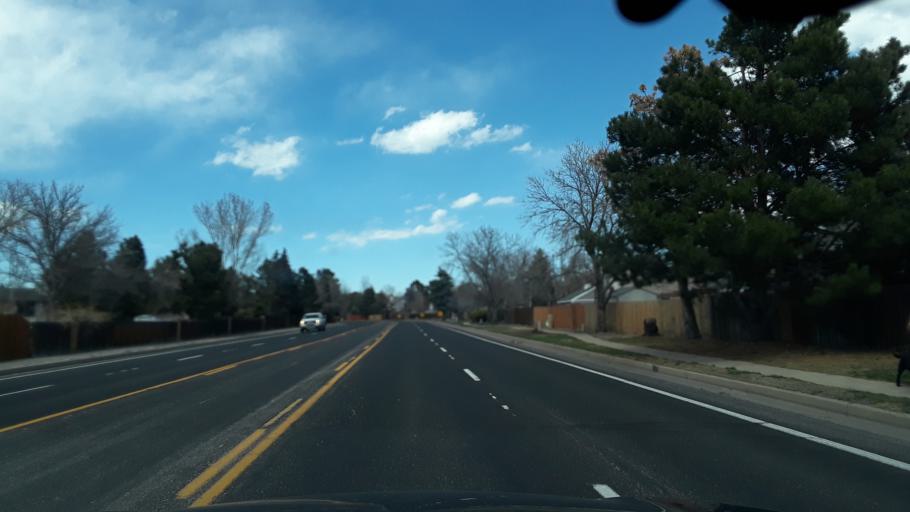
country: US
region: Colorado
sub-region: El Paso County
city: Black Forest
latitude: 38.9490
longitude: -104.7521
